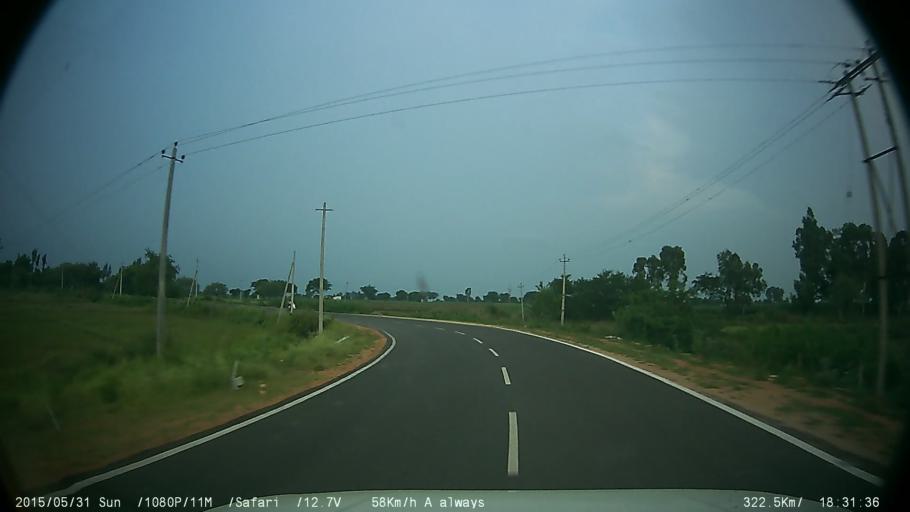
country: IN
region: Karnataka
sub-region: Mysore
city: Nanjangud
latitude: 12.1277
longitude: 76.7455
